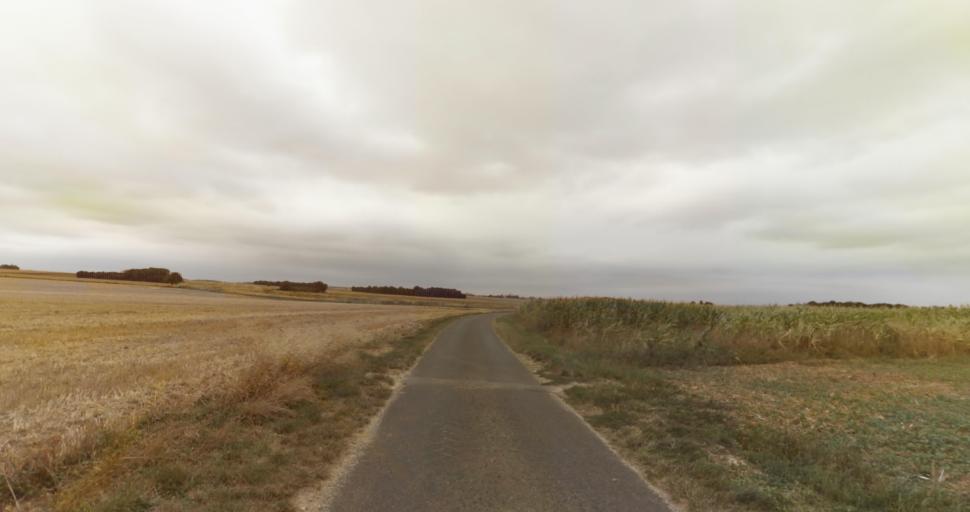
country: FR
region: Haute-Normandie
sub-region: Departement de l'Eure
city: La Couture-Boussey
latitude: 48.9140
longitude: 1.3493
